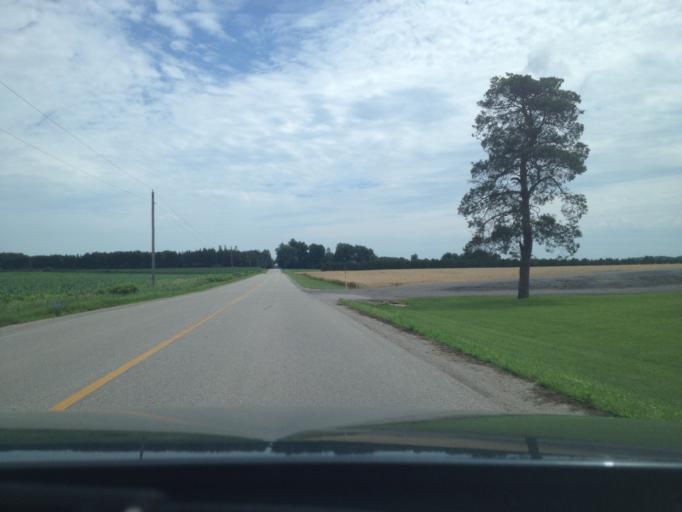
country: CA
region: Ontario
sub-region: Oxford County
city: Woodstock
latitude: 42.9954
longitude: -80.6433
